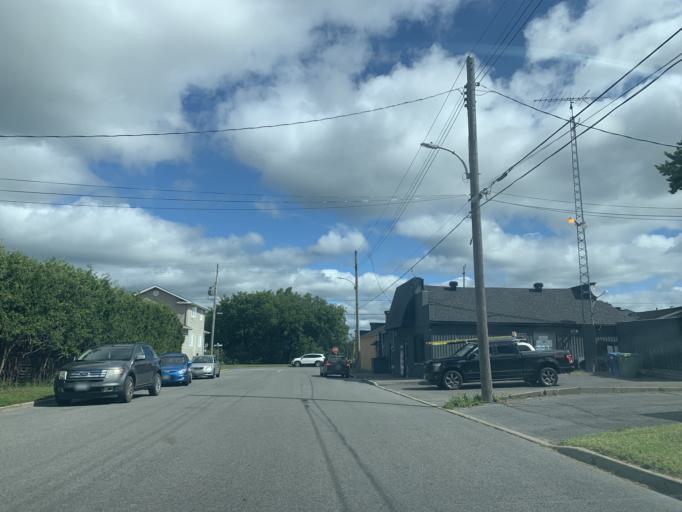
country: CA
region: Ontario
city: Hawkesbury
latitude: 45.6071
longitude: -74.5867
